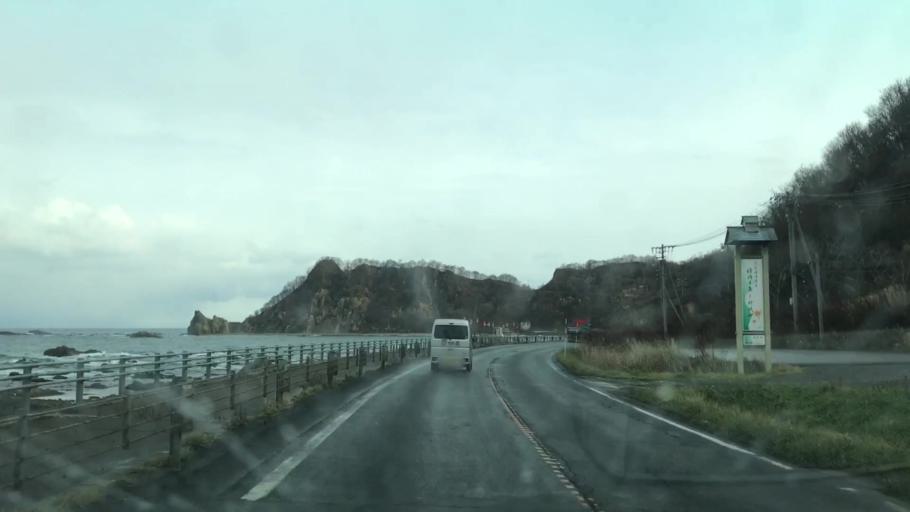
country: JP
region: Hokkaido
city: Yoichi
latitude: 43.2965
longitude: 140.6187
